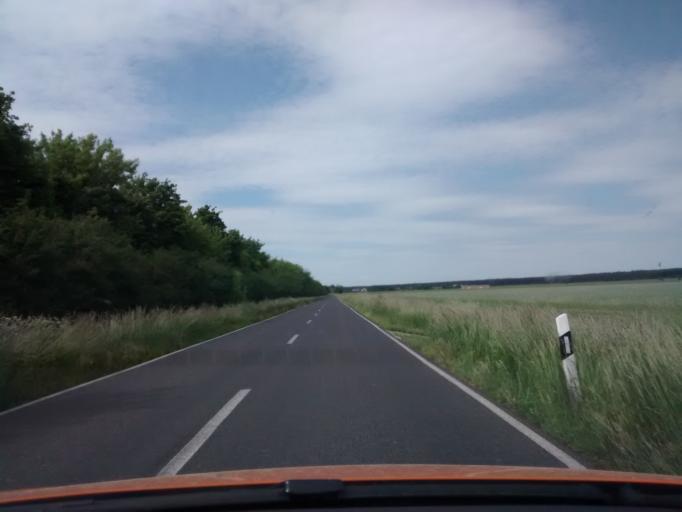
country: DE
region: Brandenburg
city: Ihlow
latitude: 51.9414
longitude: 13.3342
